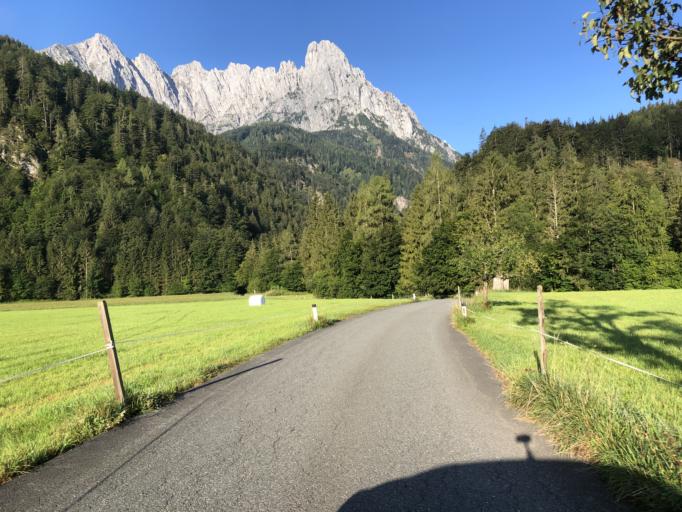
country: AT
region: Tyrol
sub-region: Politischer Bezirk Kitzbuhel
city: Schwendt
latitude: 47.5802
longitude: 12.3874
